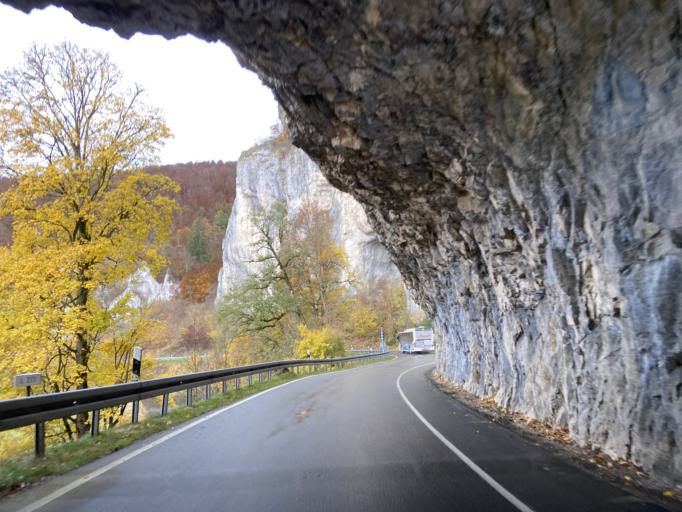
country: DE
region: Baden-Wuerttemberg
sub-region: Tuebingen Region
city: Stetten am Kalten Markt
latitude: 48.0926
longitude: 9.1079
